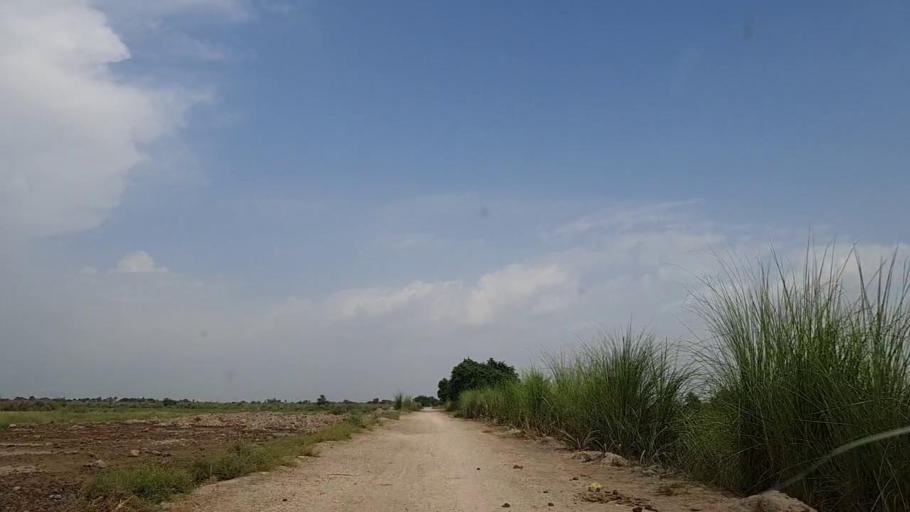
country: PK
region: Sindh
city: Khanpur
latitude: 27.8233
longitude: 69.5220
